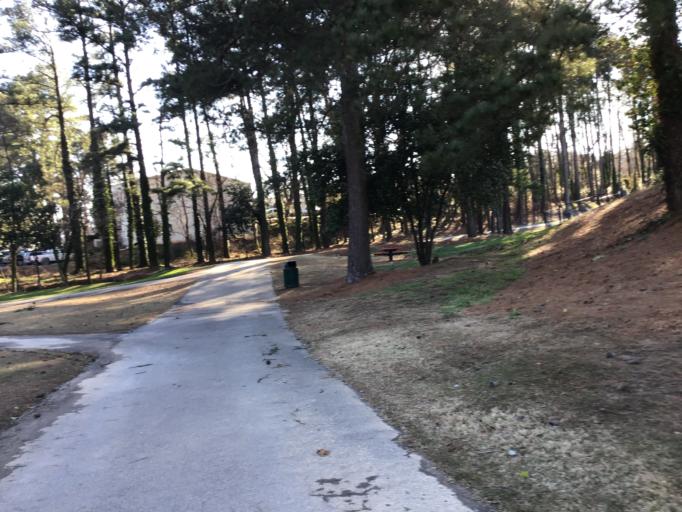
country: US
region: Georgia
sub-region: DeKalb County
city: Chamblee
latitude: 33.8660
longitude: -84.2963
